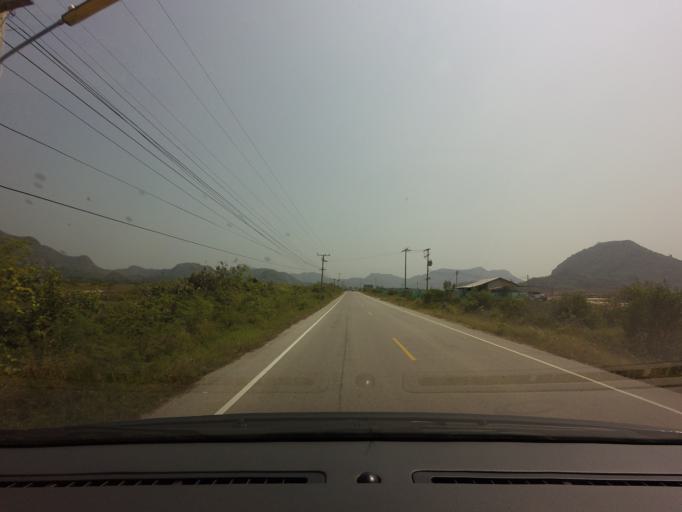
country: TH
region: Prachuap Khiri Khan
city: Sam Roi Yot
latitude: 12.1959
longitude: 99.9811
